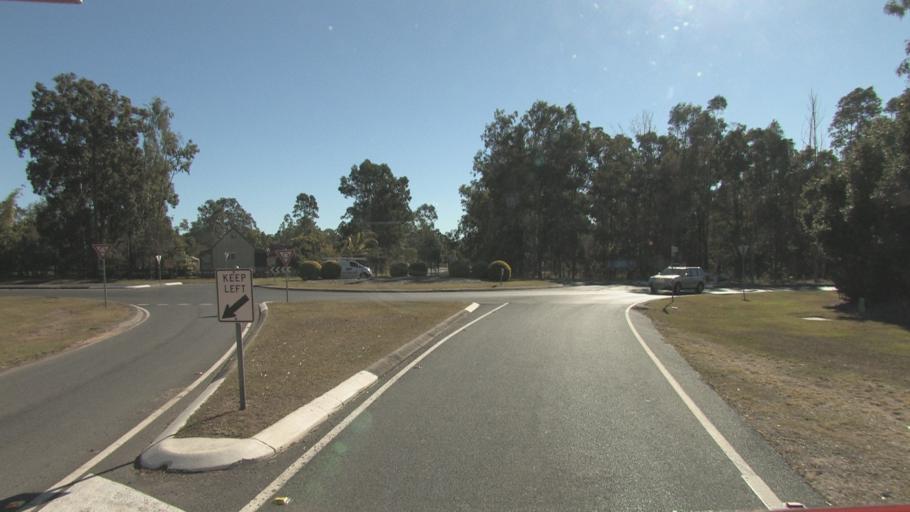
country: AU
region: Queensland
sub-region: Logan
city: North Maclean
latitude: -27.7373
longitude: 152.9702
